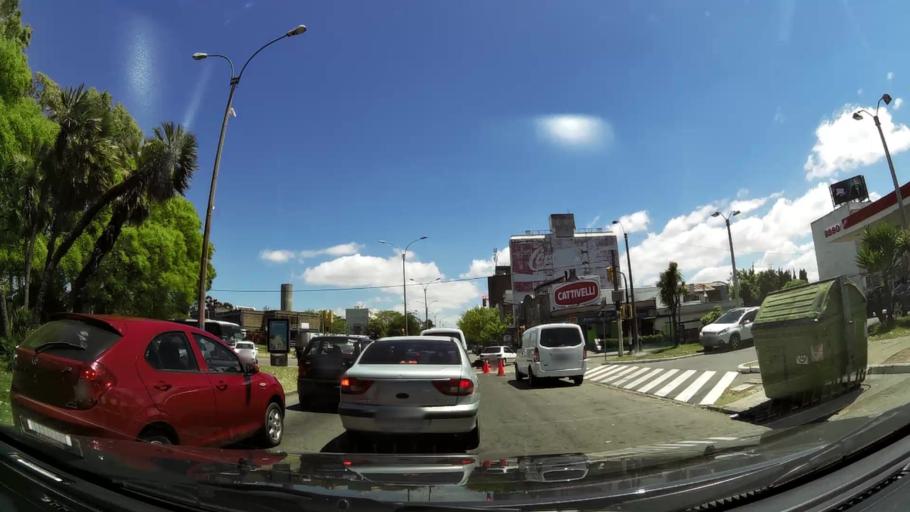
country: UY
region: Montevideo
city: Montevideo
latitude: -34.8977
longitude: -56.1244
